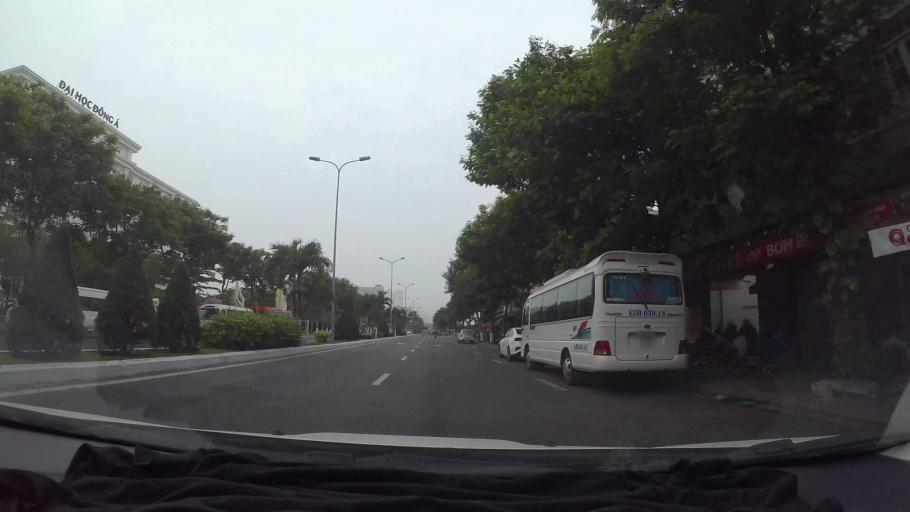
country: VN
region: Da Nang
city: Cam Le
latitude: 16.0328
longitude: 108.2217
